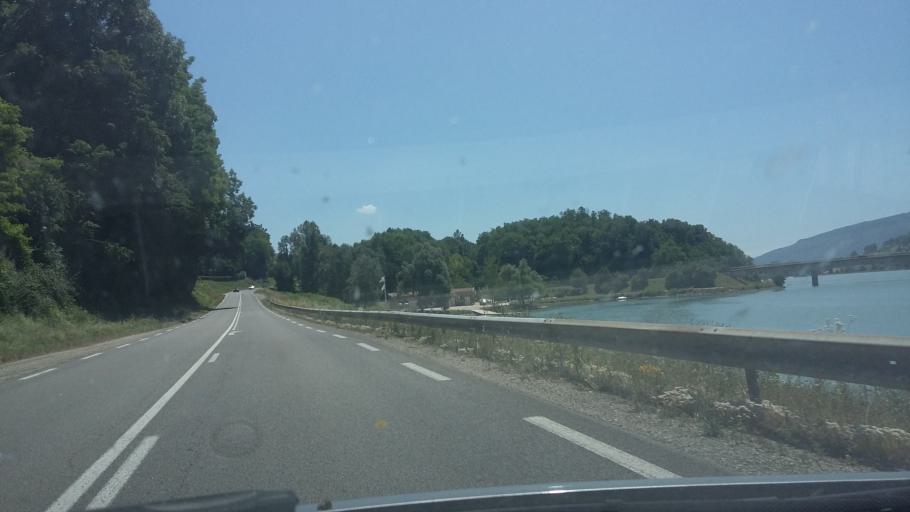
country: FR
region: Rhone-Alpes
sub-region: Departement de l'Ain
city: Belley
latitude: 45.7407
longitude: 5.7071
